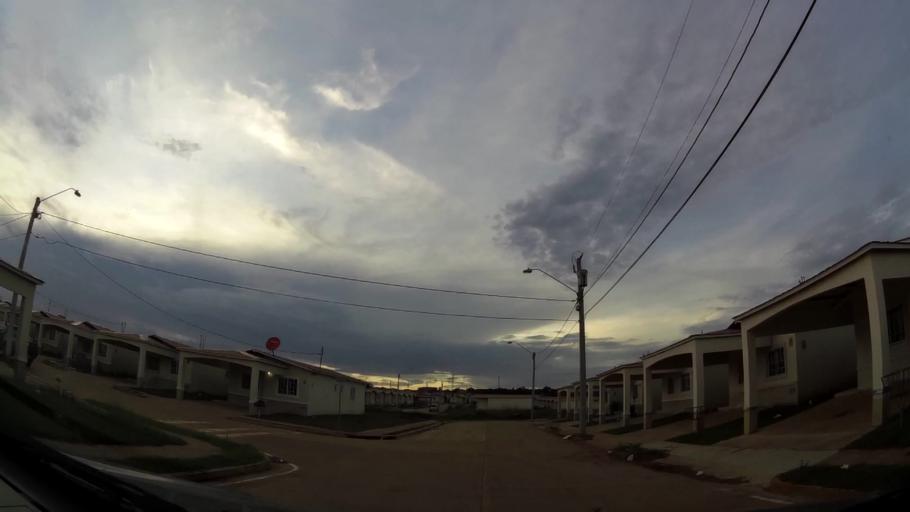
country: PA
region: Panama
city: La Mitra
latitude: 8.8567
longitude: -79.7561
